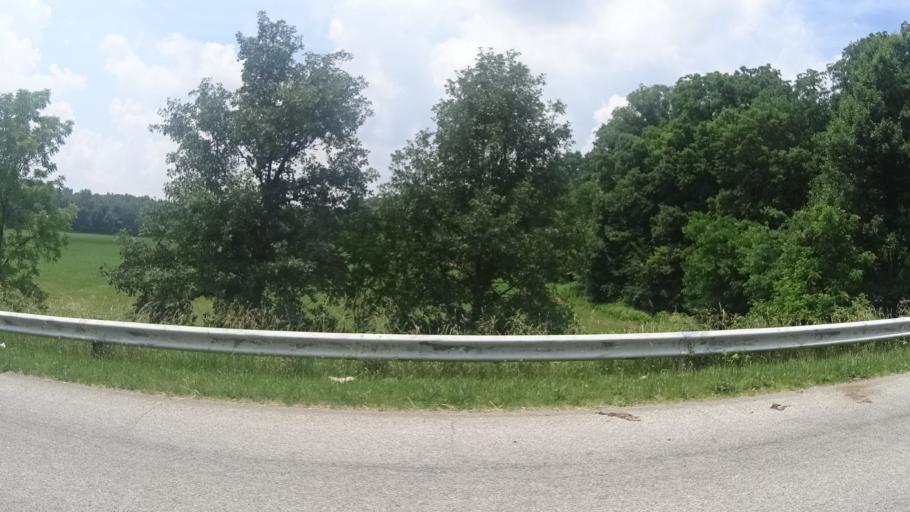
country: US
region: Ohio
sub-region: Huron County
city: Monroeville
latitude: 41.2913
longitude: -82.6647
